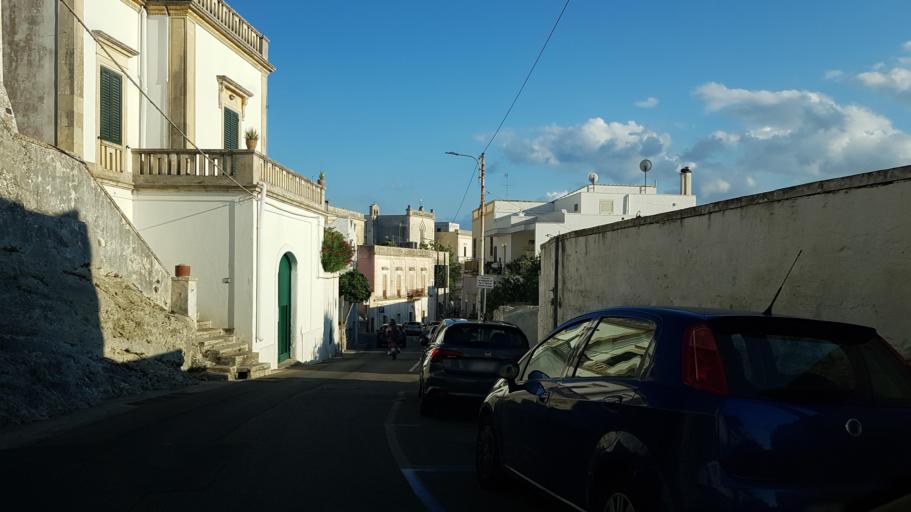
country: IT
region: Apulia
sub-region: Provincia di Lecce
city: Castro
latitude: 40.0040
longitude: 18.4253
